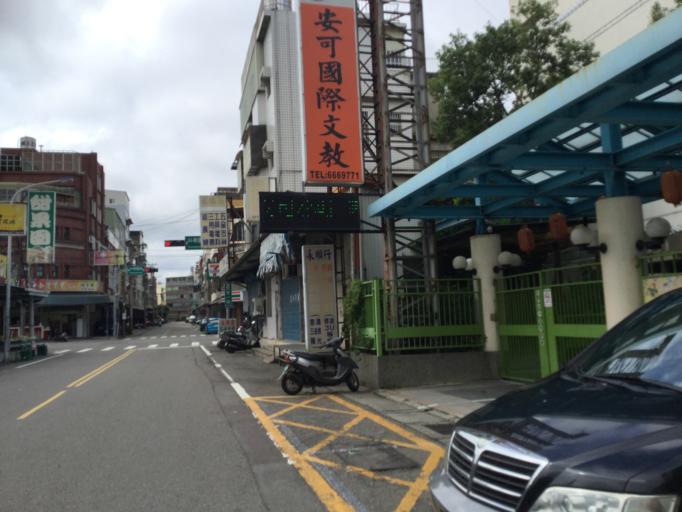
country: TW
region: Taiwan
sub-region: Hsinchu
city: Hsinchu
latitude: 24.7833
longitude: 121.0120
